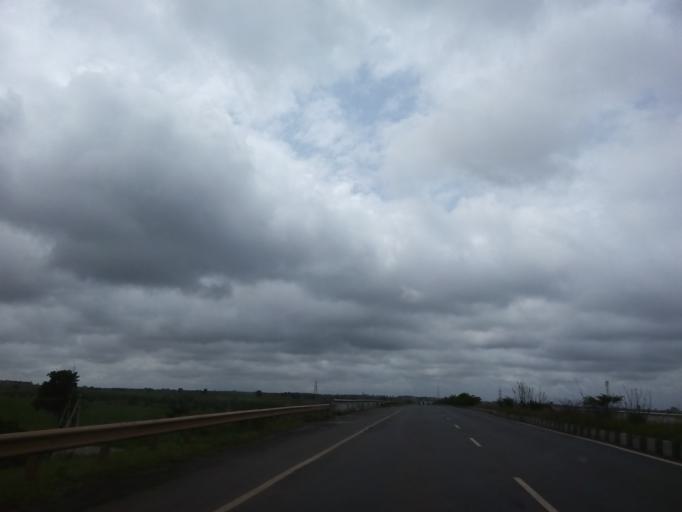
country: IN
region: Karnataka
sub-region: Haveri
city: Haveri
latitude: 14.8393
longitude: 75.3528
